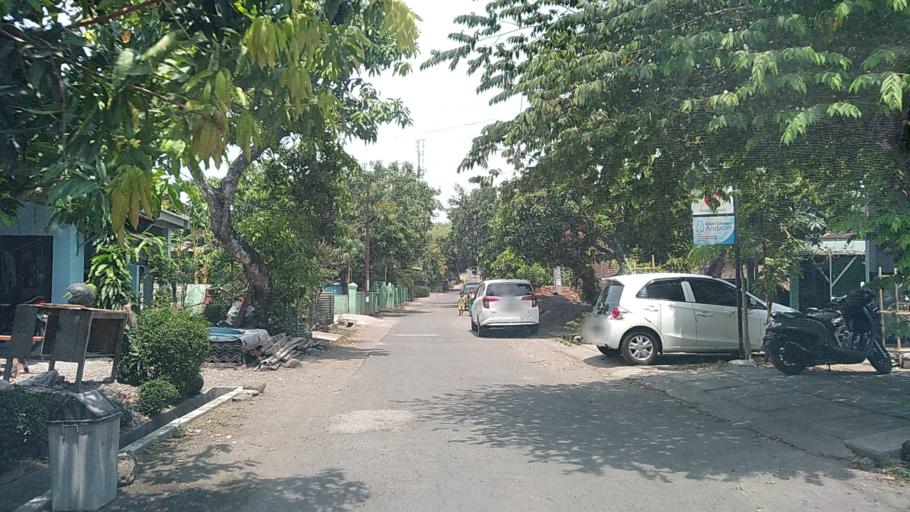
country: ID
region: Central Java
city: Mranggen
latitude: -7.0533
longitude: 110.4795
